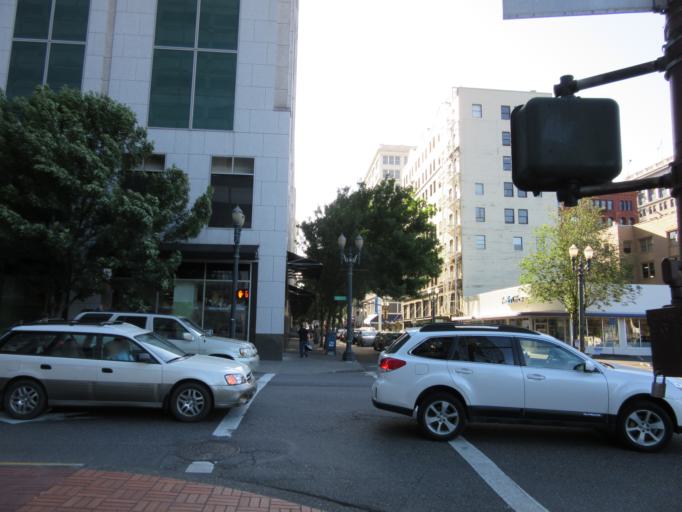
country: US
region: Oregon
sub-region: Multnomah County
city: Portland
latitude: 45.5186
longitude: -122.6742
